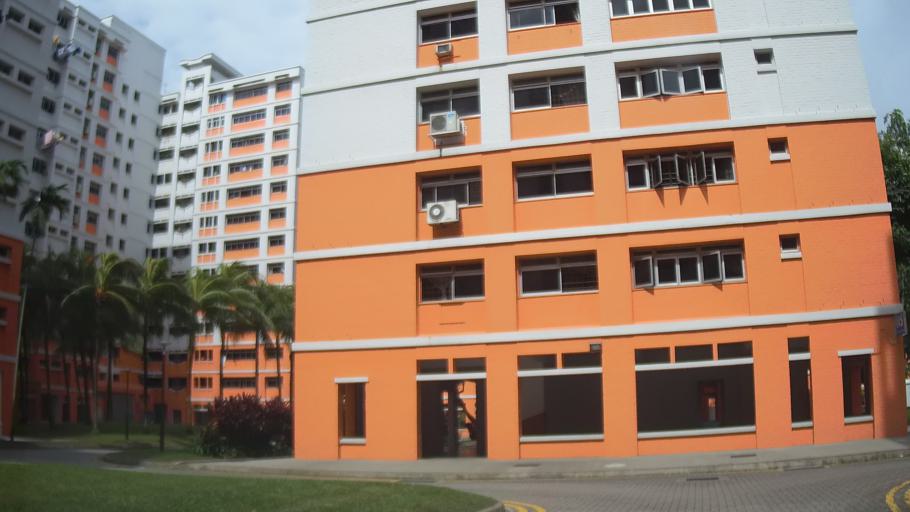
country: MY
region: Johor
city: Johor Bahru
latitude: 1.3931
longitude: 103.7440
